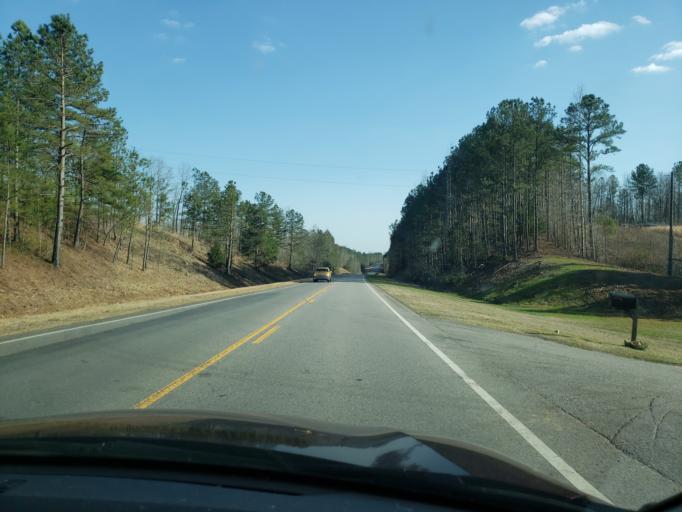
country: US
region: Alabama
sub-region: Randolph County
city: Wedowee
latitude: 33.4361
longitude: -85.5591
